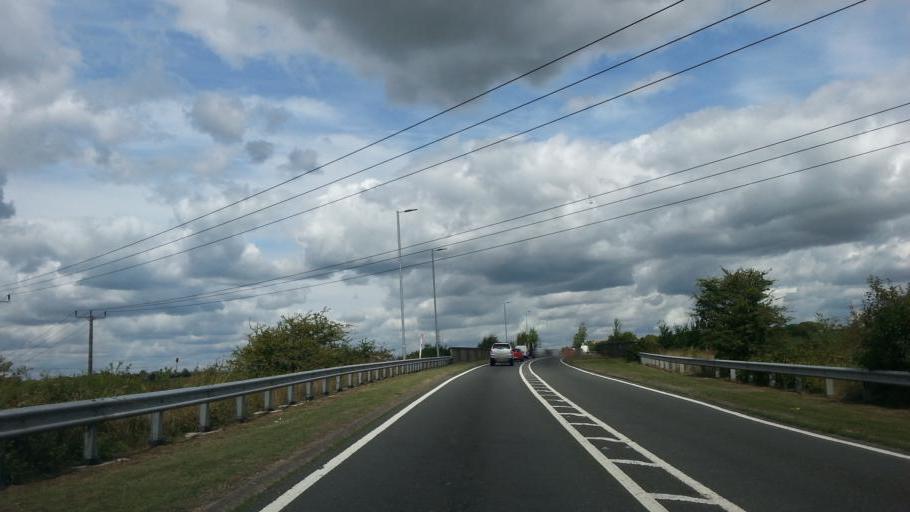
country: GB
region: England
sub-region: Essex
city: South Benfleet
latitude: 51.5534
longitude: 0.5388
